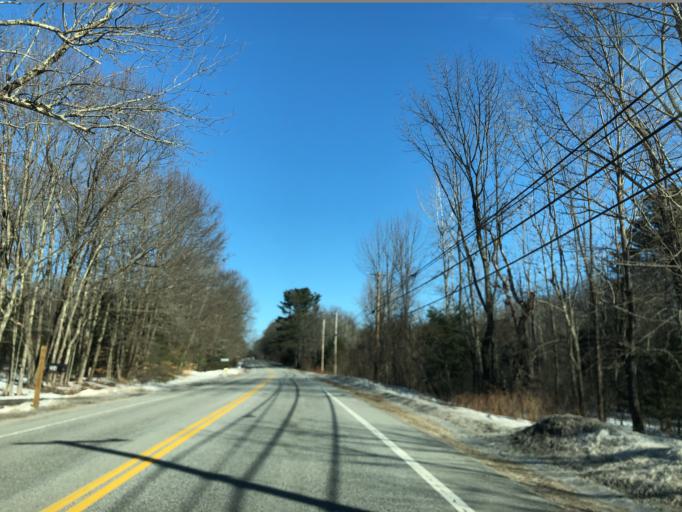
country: US
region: Maine
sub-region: Cumberland County
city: South Windham
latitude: 43.7621
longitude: -70.4231
